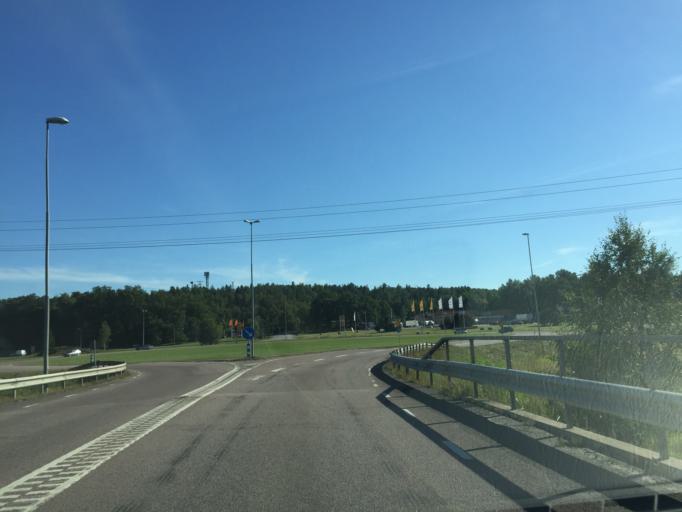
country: SE
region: Vaestmanland
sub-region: Arboga Kommun
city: Arboga
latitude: 59.3985
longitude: 15.8889
